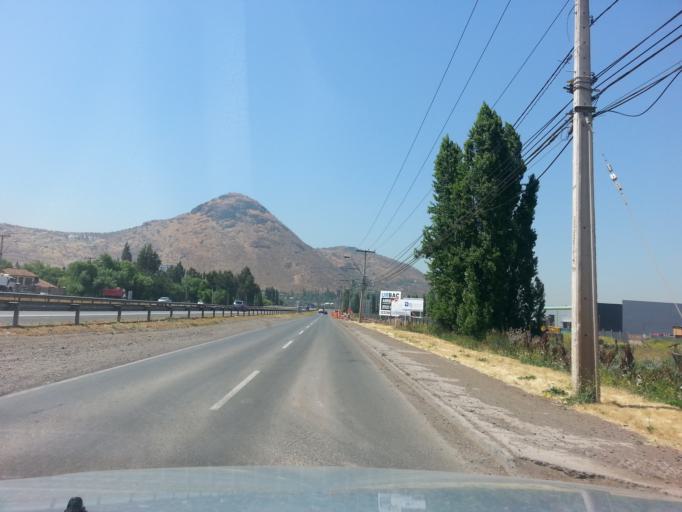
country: CL
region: Santiago Metropolitan
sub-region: Provincia de Chacabuco
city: Chicureo Abajo
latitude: -33.2955
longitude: -70.7016
